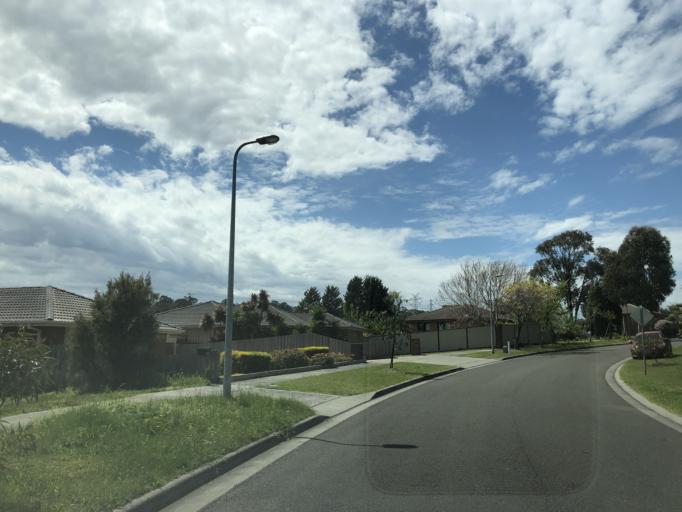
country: AU
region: Victoria
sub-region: Casey
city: Endeavour Hills
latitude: -37.9639
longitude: 145.2662
